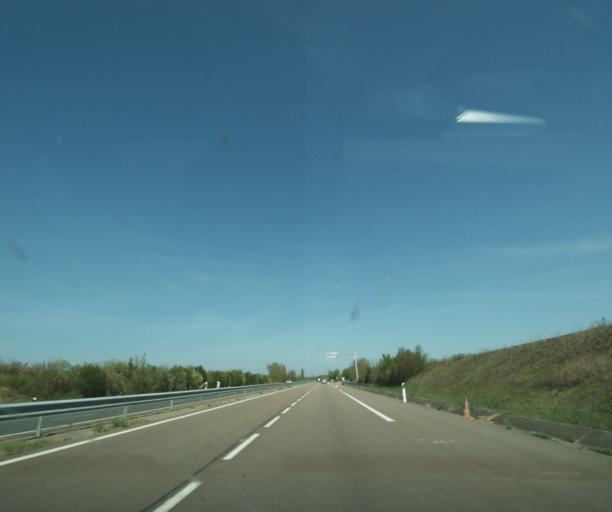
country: FR
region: Bourgogne
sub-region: Departement de la Nievre
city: La Charite-sur-Loire
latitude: 47.1534
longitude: 3.0487
